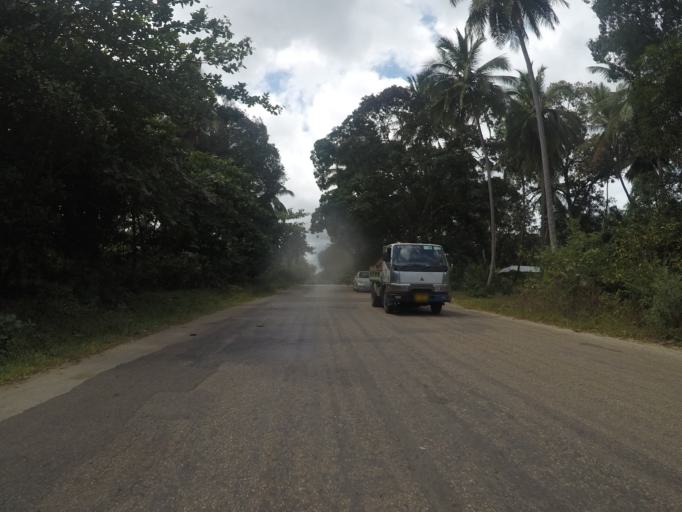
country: TZ
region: Zanzibar Central/South
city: Koani
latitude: -6.2019
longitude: 39.3213
